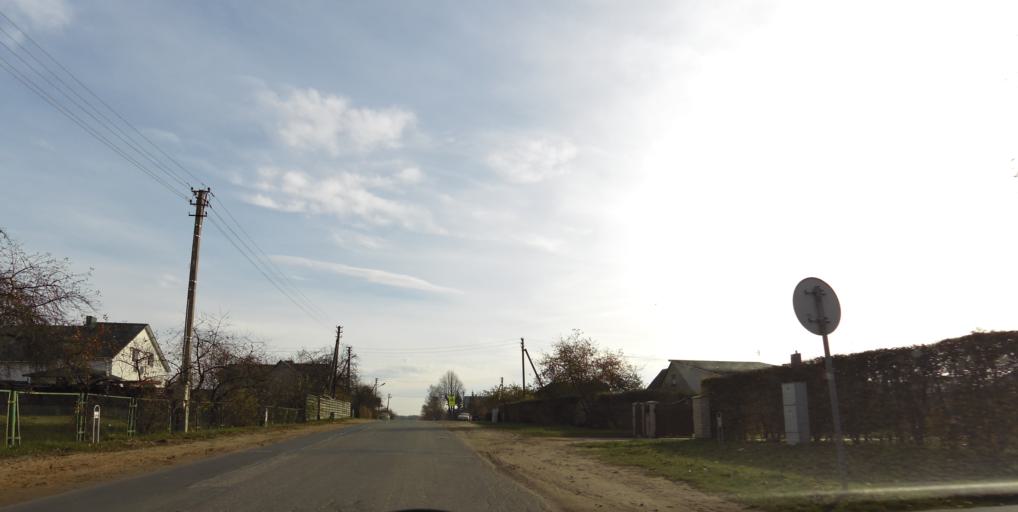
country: LT
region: Vilnius County
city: Pilaite
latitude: 54.7255
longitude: 25.1845
